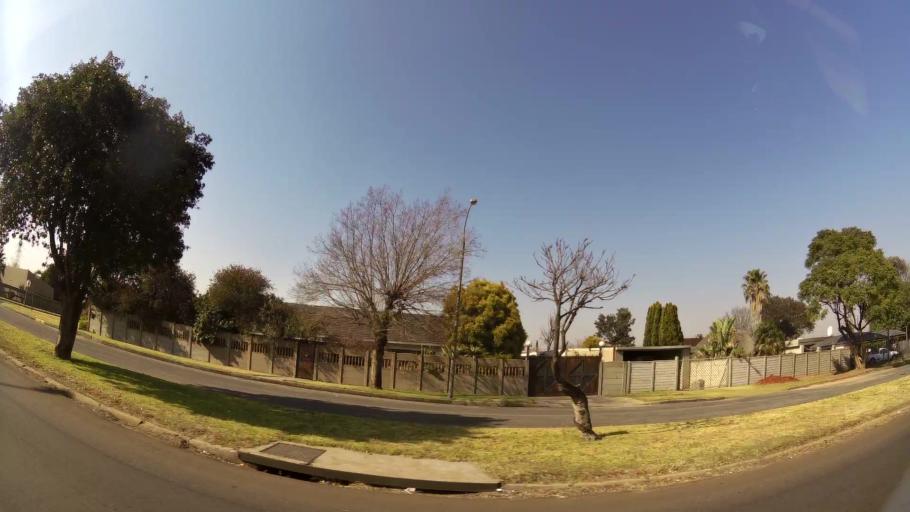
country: ZA
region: Gauteng
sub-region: Ekurhuleni Metropolitan Municipality
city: Boksburg
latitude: -26.2295
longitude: 28.2737
